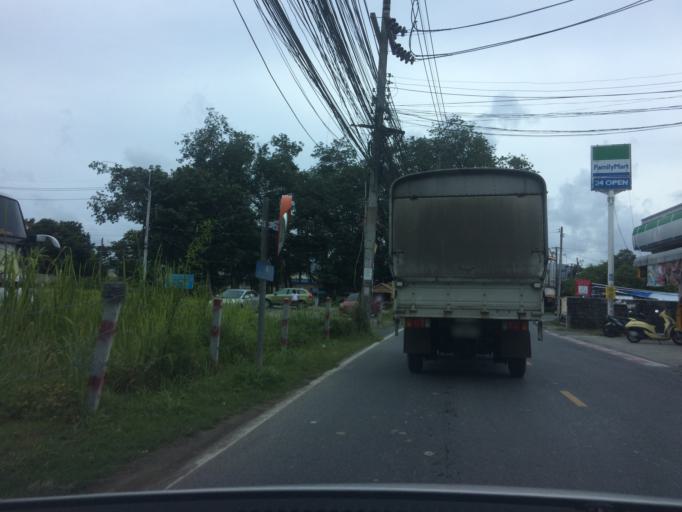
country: TH
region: Phuket
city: Mueang Phuket
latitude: 7.8621
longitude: 98.3644
